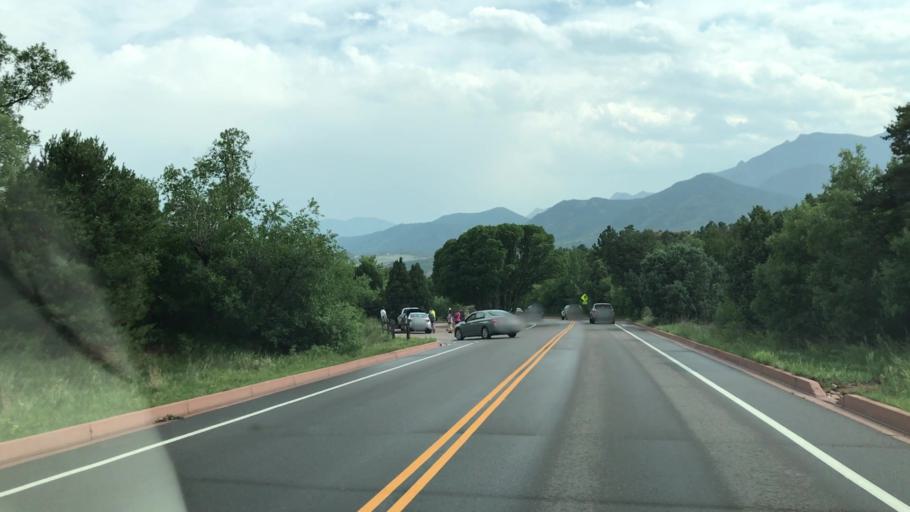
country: US
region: Colorado
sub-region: El Paso County
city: Manitou Springs
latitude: 38.8738
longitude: -104.8852
